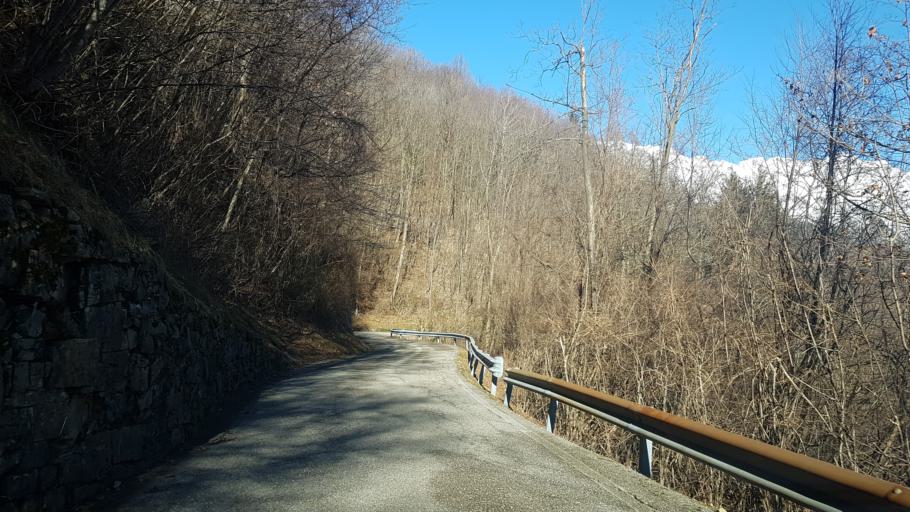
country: IT
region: Friuli Venezia Giulia
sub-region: Provincia di Udine
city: Isola
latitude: 46.2599
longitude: 13.2014
